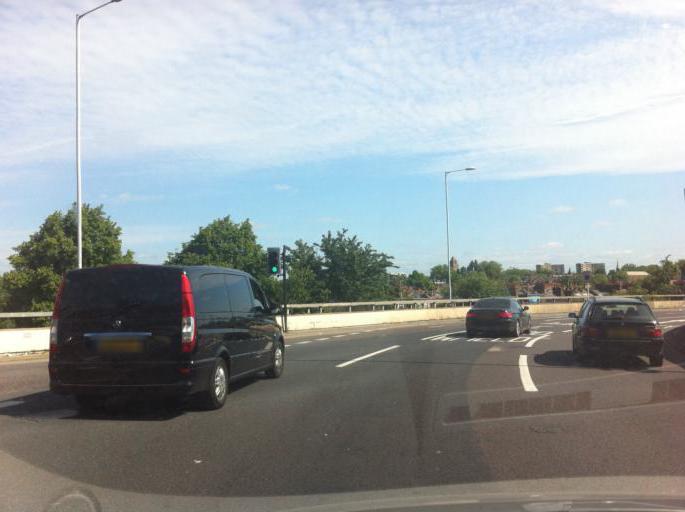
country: GB
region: England
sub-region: Greater London
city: Hammersmith
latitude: 51.5153
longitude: -0.2215
